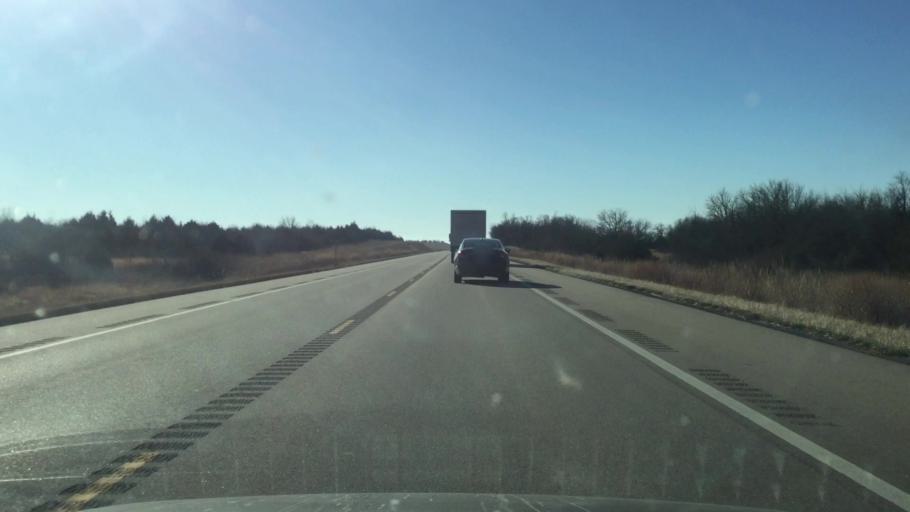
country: US
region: Kansas
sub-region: Allen County
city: Iola
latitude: 38.0365
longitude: -95.3806
